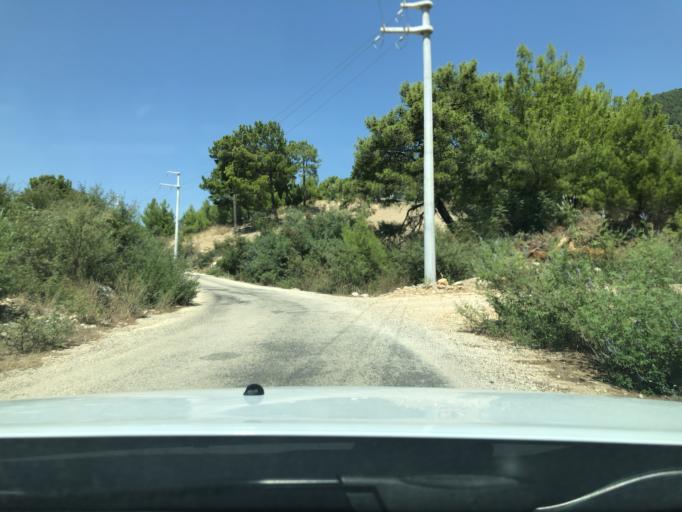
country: TR
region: Antalya
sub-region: Manavgat
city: Manavgat
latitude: 36.8791
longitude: 31.5512
